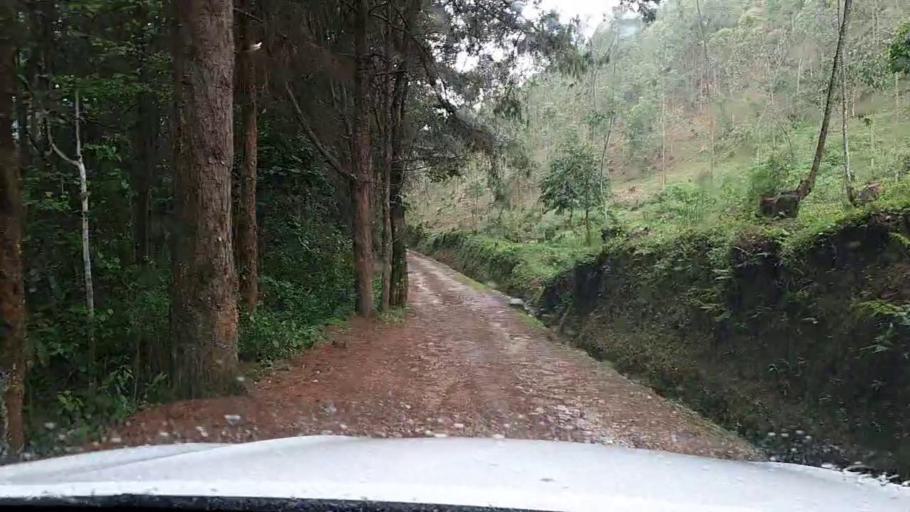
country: RW
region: Western Province
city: Cyangugu
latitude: -2.5533
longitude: 28.9774
